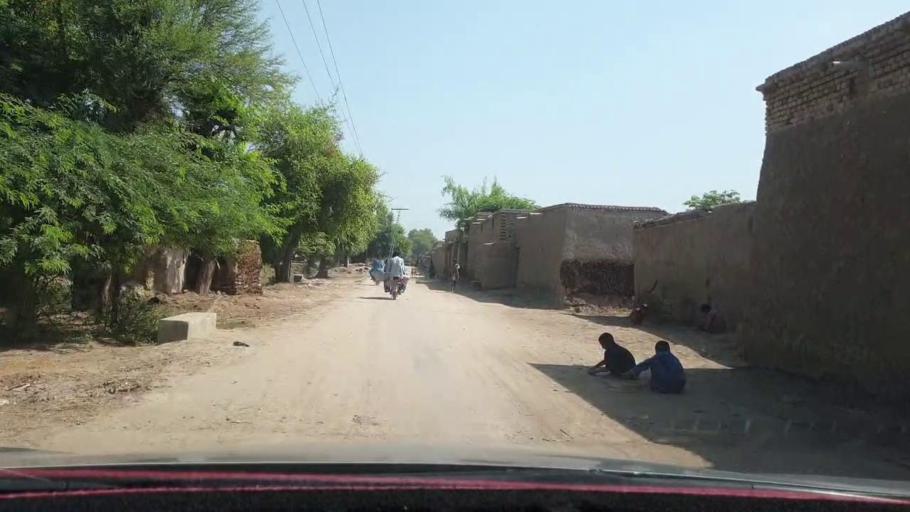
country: PK
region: Sindh
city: Warah
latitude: 27.4817
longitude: 67.8293
